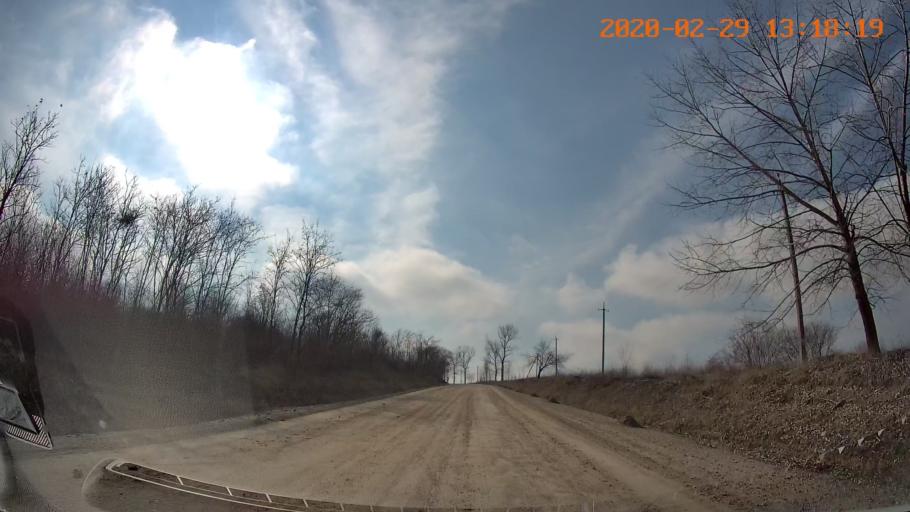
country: MD
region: Telenesti
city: Camenca
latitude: 47.9941
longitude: 28.6588
